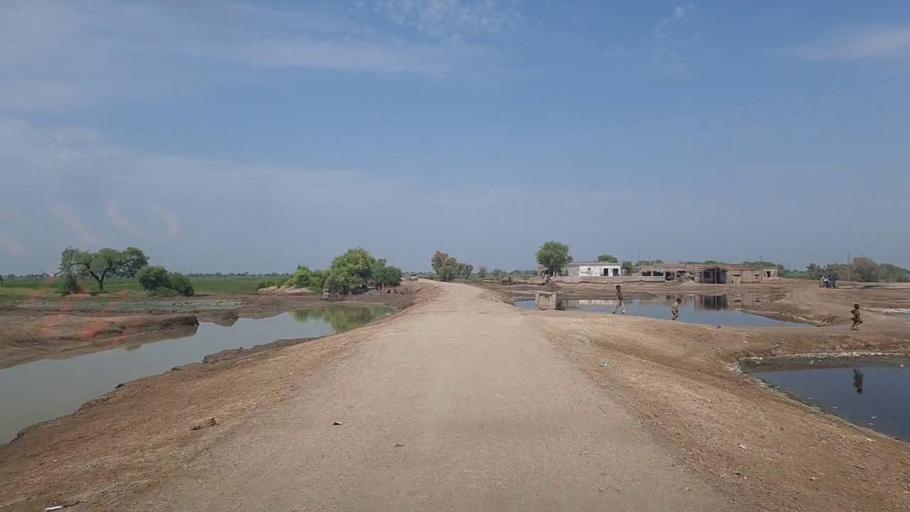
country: PK
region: Sindh
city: Thul
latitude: 28.2941
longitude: 68.6819
